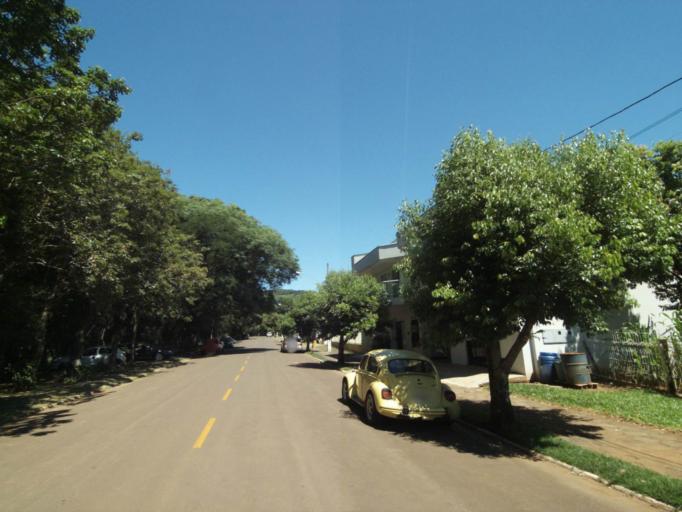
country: BR
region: Parana
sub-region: Ampere
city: Ampere
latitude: -26.1720
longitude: -53.3618
